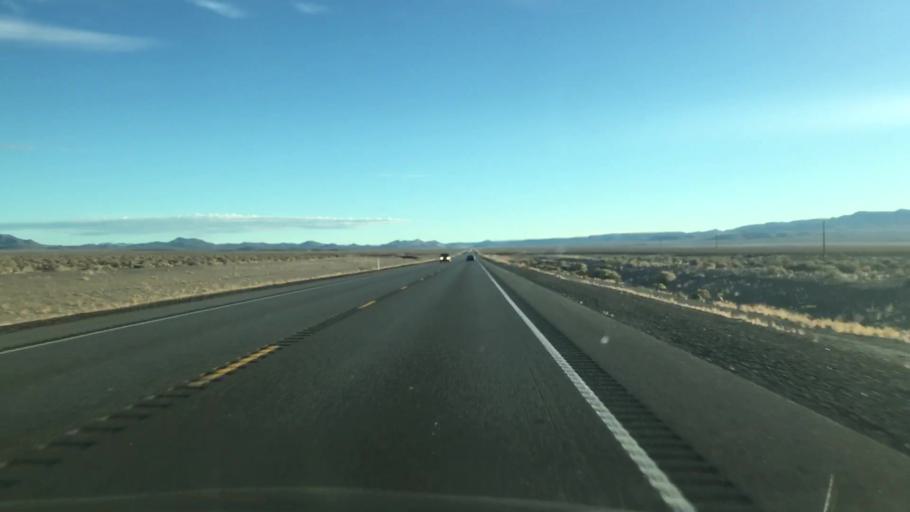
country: US
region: Nevada
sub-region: Esmeralda County
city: Goldfield
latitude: 37.8695
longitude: -117.2421
